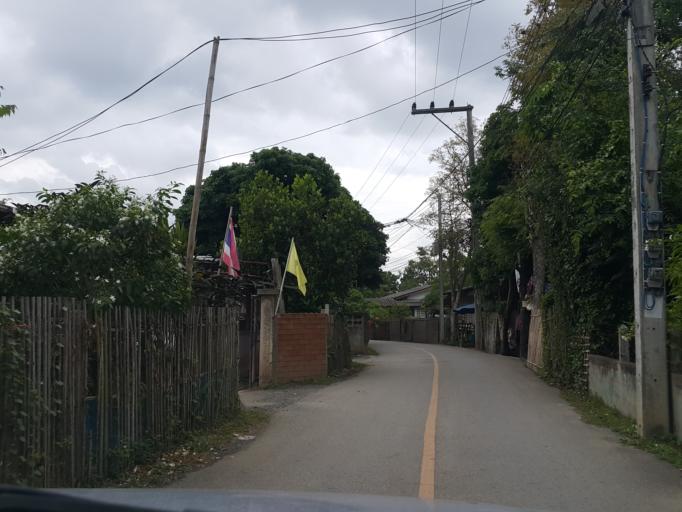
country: TH
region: Chiang Mai
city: San Kamphaeng
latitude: 18.7912
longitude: 99.1108
